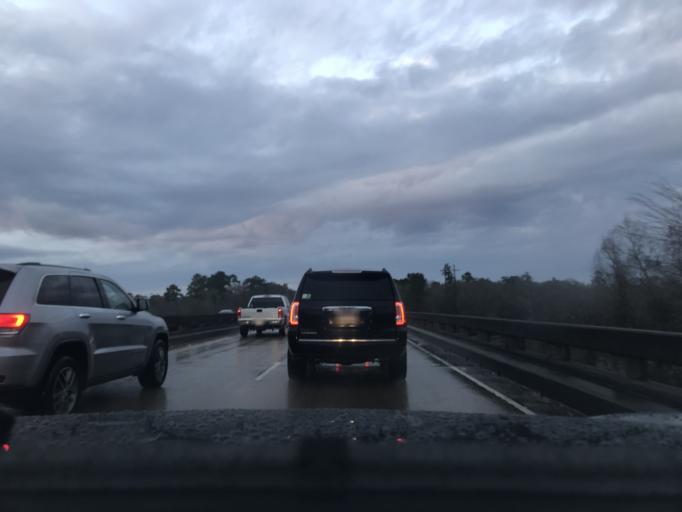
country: US
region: Louisiana
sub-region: Calcasieu Parish
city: Moss Bluff
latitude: 30.2713
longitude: -93.1821
